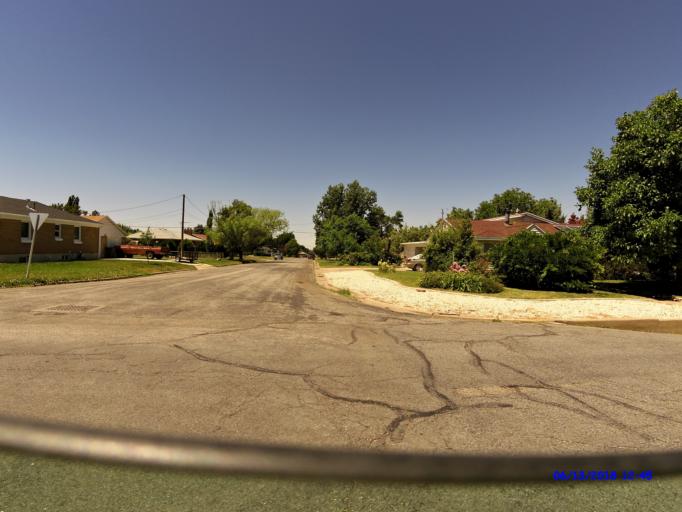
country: US
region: Utah
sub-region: Weber County
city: South Ogden
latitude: 41.2016
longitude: -111.9514
